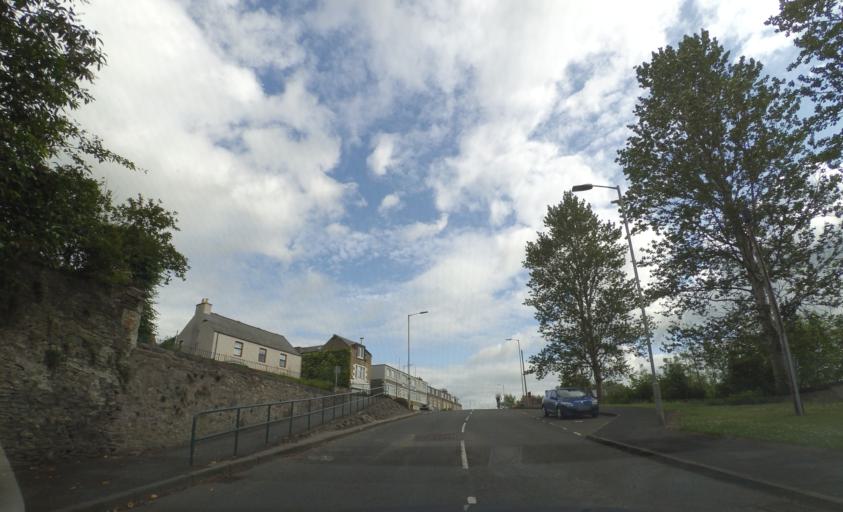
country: GB
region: Scotland
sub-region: The Scottish Borders
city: Hawick
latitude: 55.4253
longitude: -2.7909
